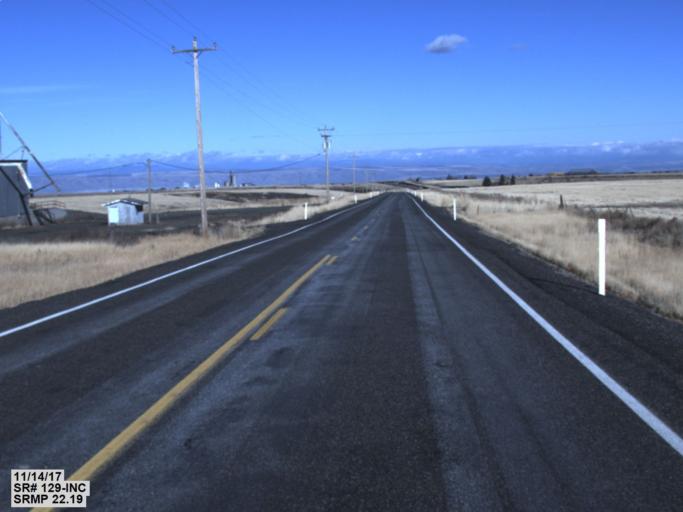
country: US
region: Washington
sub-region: Asotin County
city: Asotin
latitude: 46.1880
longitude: -117.0782
